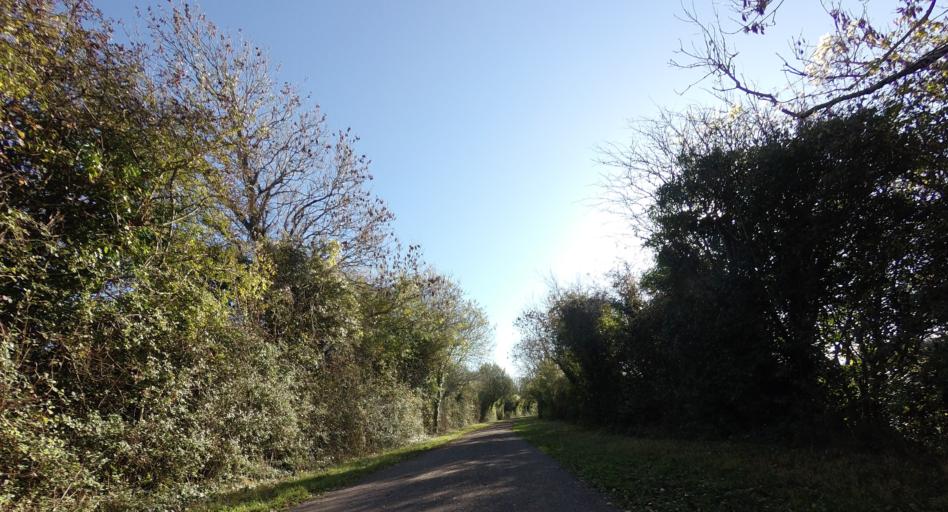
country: GB
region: England
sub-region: West Sussex
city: Shoreham-by-Sea
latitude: 50.8573
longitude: -0.2915
